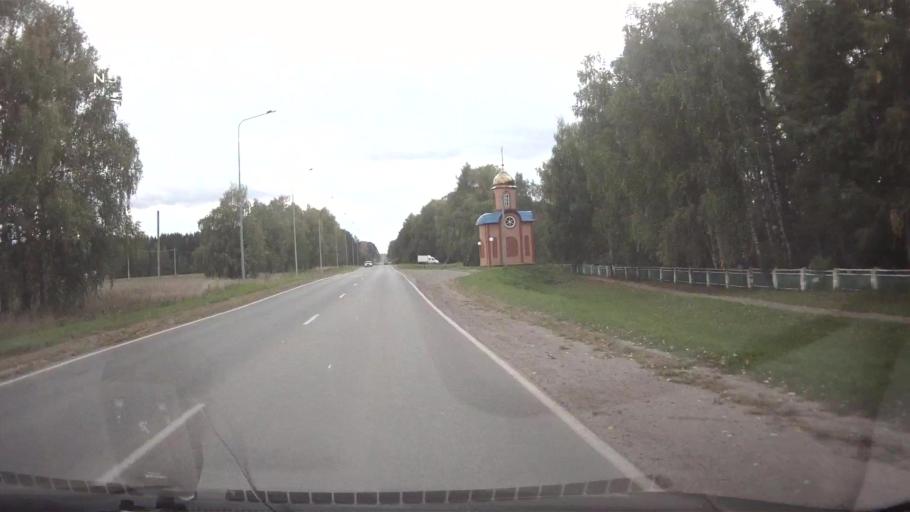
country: RU
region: Mariy-El
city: Kuzhener
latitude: 56.9937
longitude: 48.7428
